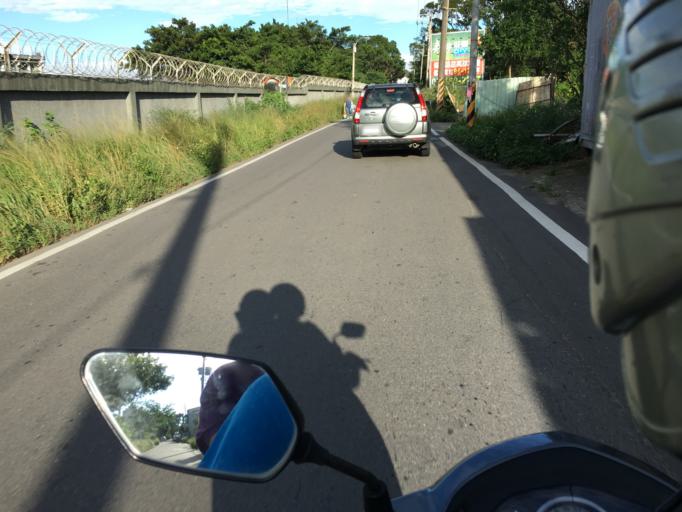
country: TW
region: Taiwan
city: Daxi
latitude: 24.8674
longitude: 121.2256
